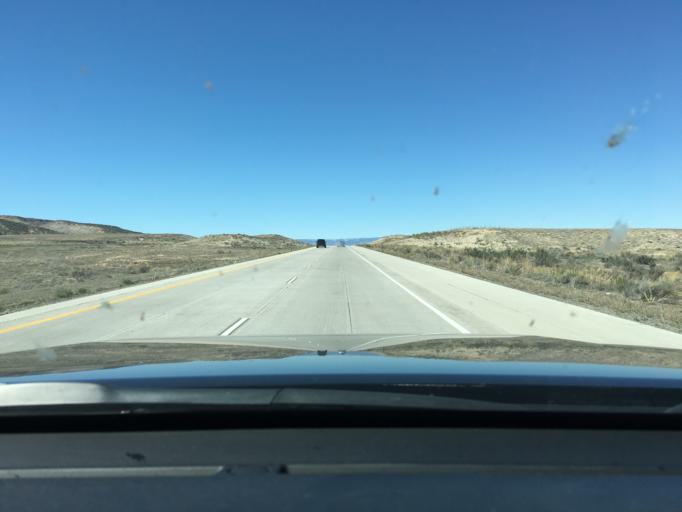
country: US
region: Colorado
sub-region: Mesa County
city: Loma
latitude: 39.1900
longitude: -108.8372
